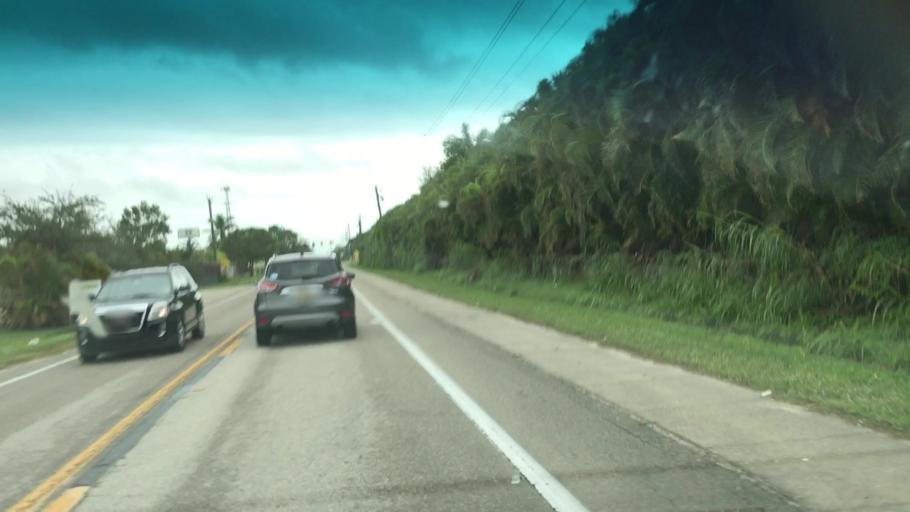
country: US
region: Florida
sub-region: Lee County
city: Harlem Heights
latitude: 26.5162
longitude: -81.9358
